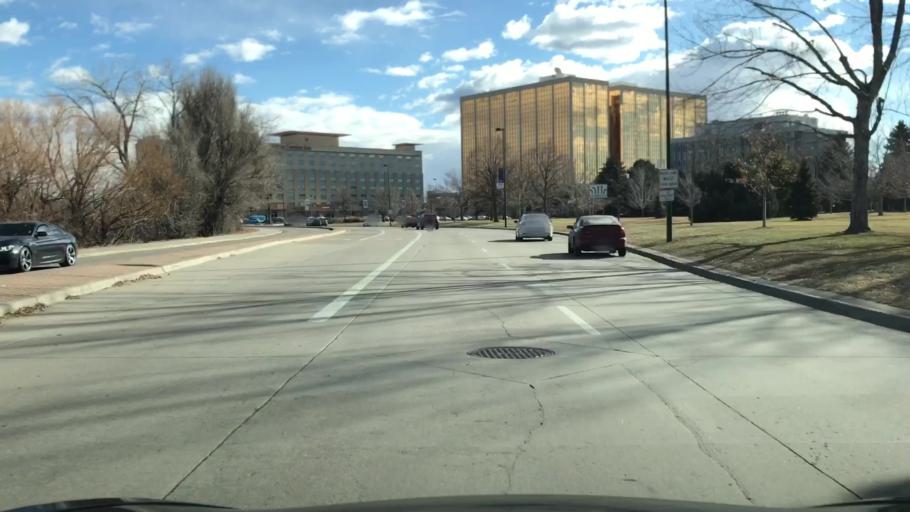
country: US
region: Colorado
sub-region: Arapahoe County
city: Glendale
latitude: 39.7069
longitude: -104.9432
